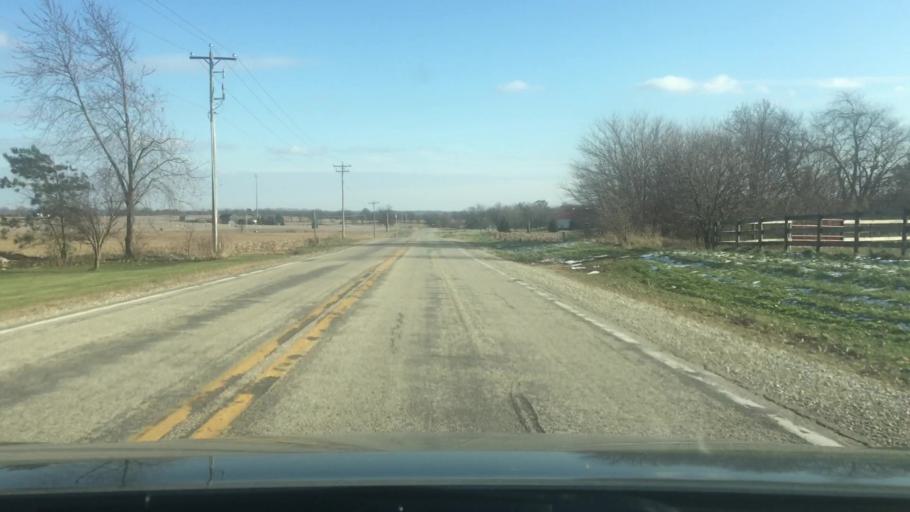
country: US
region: Wisconsin
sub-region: Jefferson County
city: Palmyra
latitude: 42.9299
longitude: -88.5669
